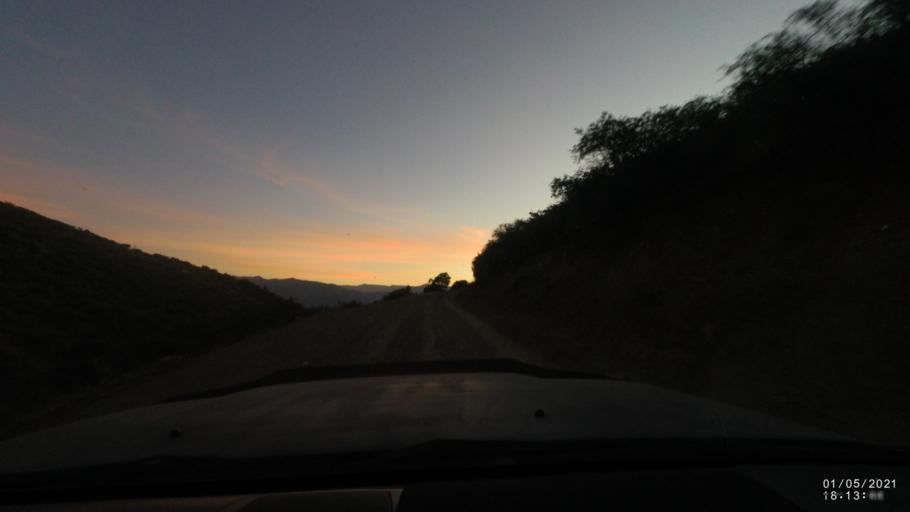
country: BO
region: Cochabamba
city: Capinota
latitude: -17.6749
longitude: -66.2083
